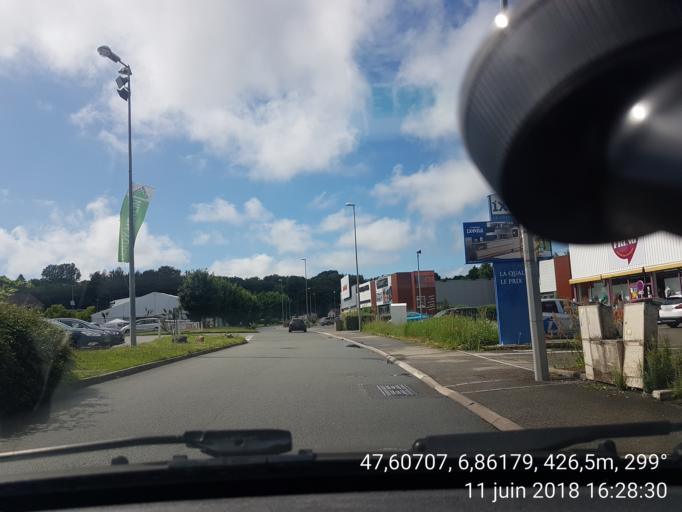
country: FR
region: Franche-Comte
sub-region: Territoire de Belfort
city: Andelnans
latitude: 47.6067
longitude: 6.8621
